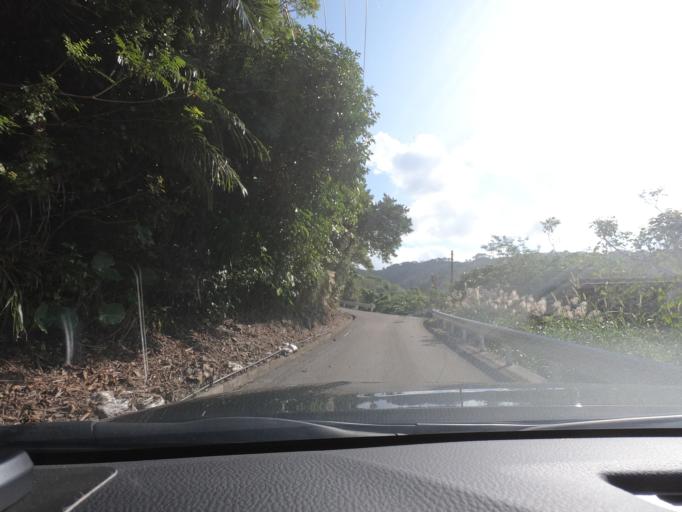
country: JP
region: Okinawa
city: Nago
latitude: 26.7571
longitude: 128.1933
